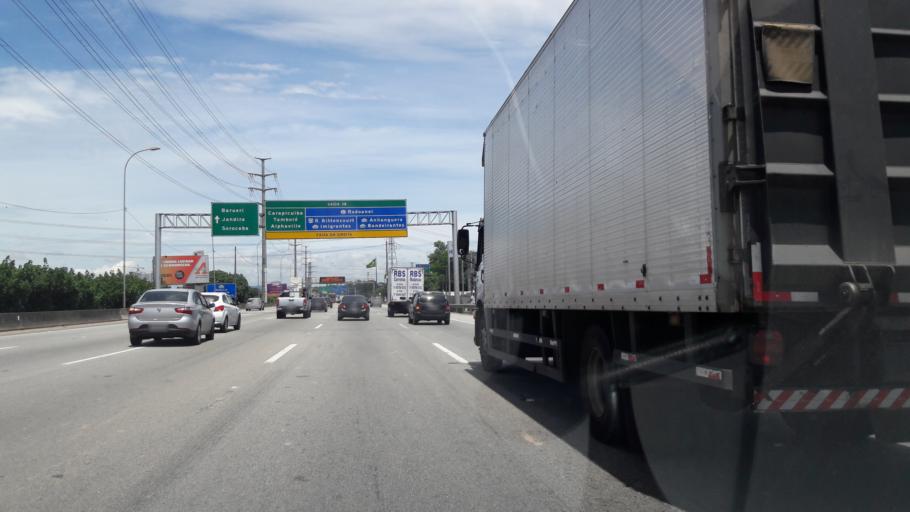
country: BR
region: Sao Paulo
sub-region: Osasco
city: Osasco
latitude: -23.5232
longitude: -46.7577
